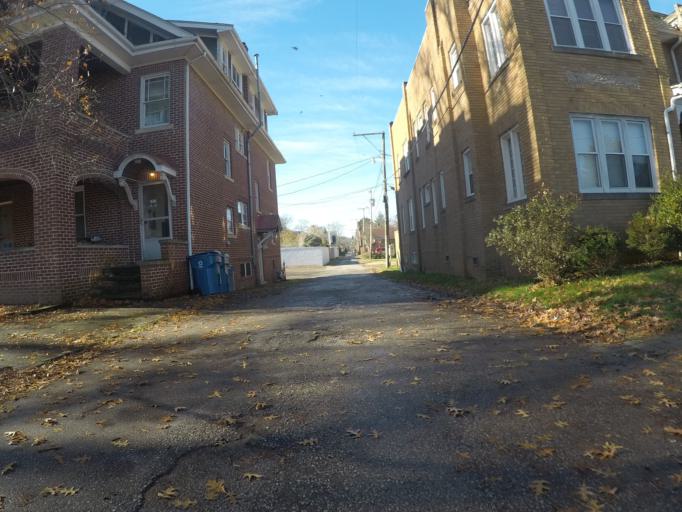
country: US
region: West Virginia
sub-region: Cabell County
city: Huntington
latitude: 38.4099
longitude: -82.4354
